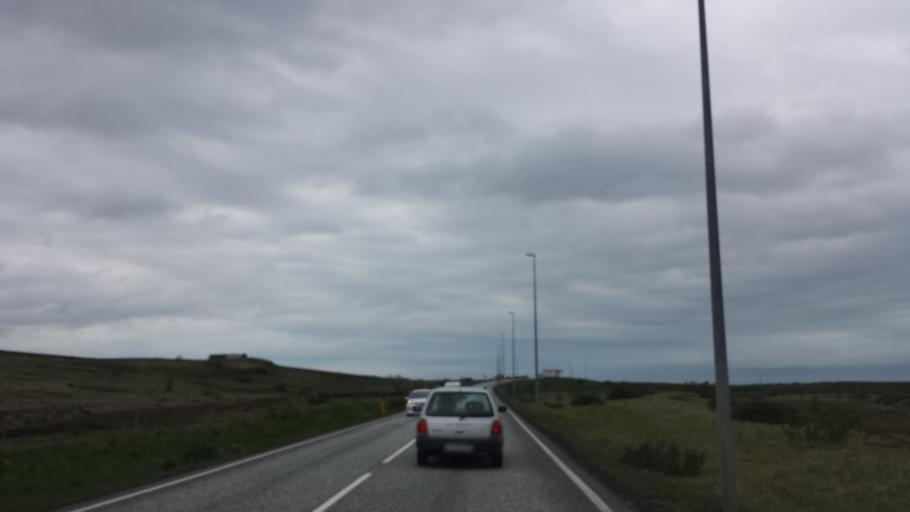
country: IS
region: Capital Region
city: Mosfellsbaer
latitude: 64.1791
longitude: -21.6612
